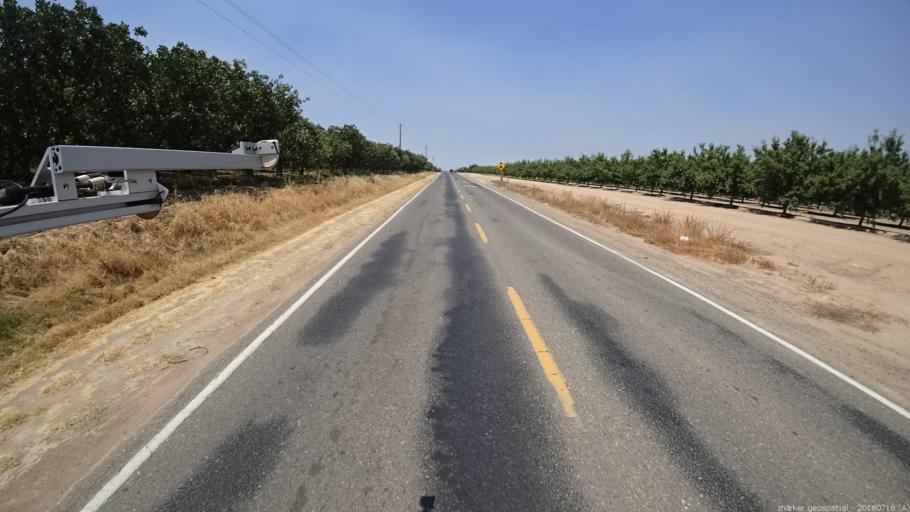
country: US
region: California
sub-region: Madera County
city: Madera Acres
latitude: 37.0544
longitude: -120.0717
